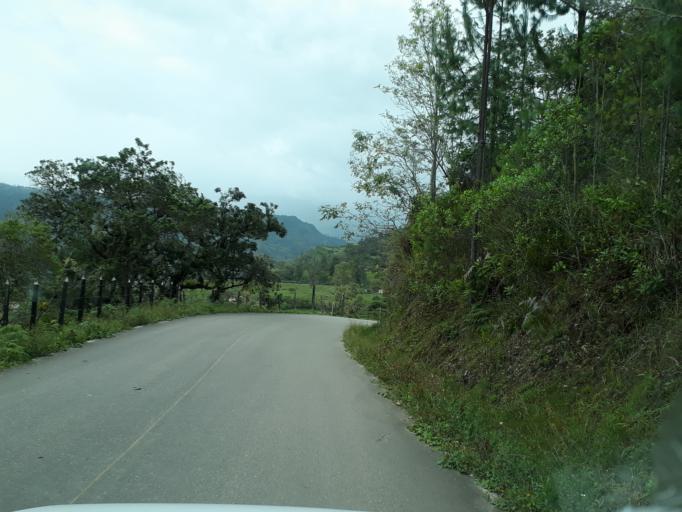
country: CO
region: Cundinamarca
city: Junin
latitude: 4.8156
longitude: -73.6741
